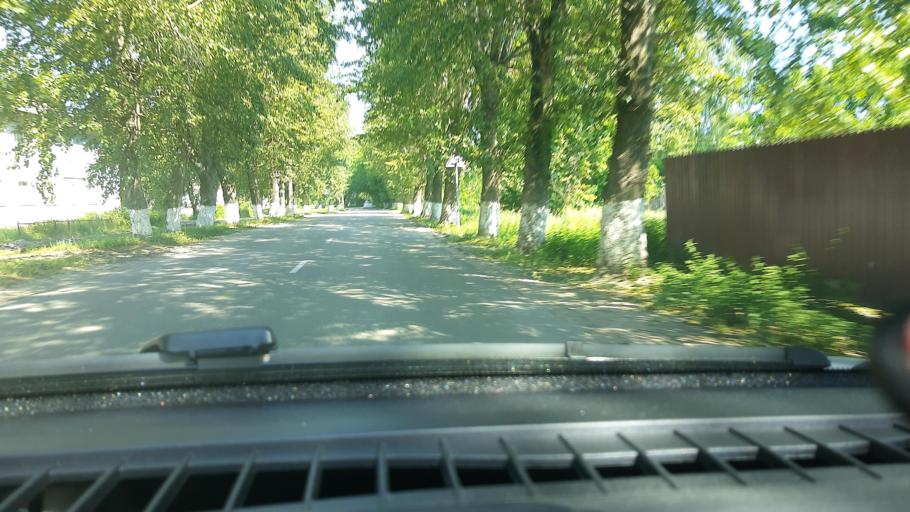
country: RU
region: Nizjnij Novgorod
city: Afonino
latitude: 56.2912
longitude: 44.1910
